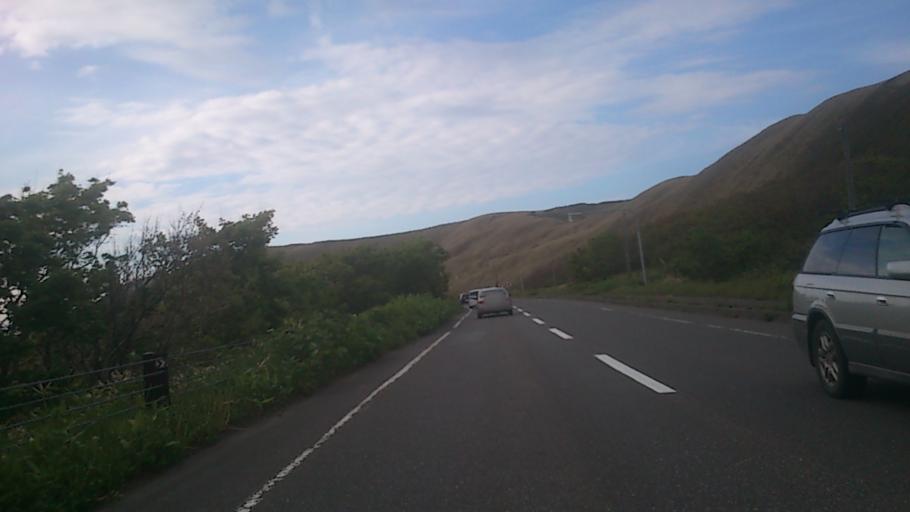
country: JP
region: Hokkaido
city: Wakkanai
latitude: 45.3663
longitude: 141.6618
